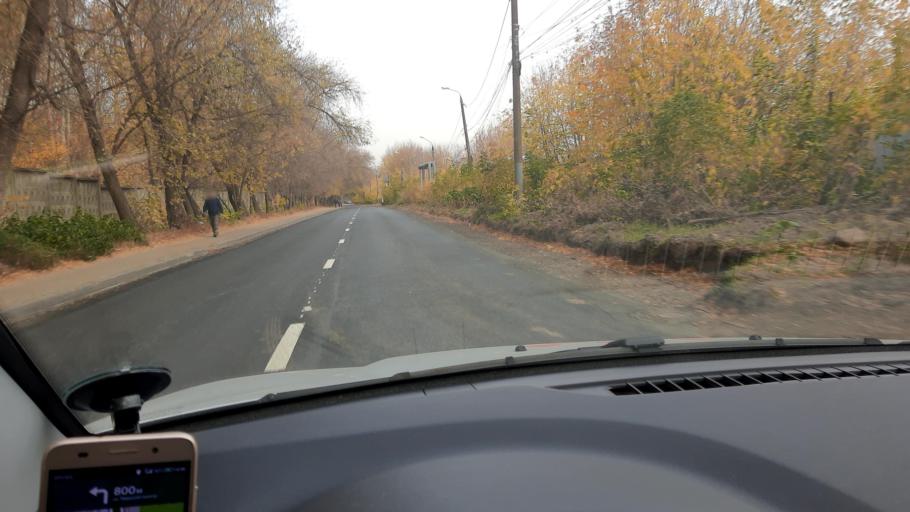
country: RU
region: Nizjnij Novgorod
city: Nizhniy Novgorod
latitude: 56.2987
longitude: 43.9988
